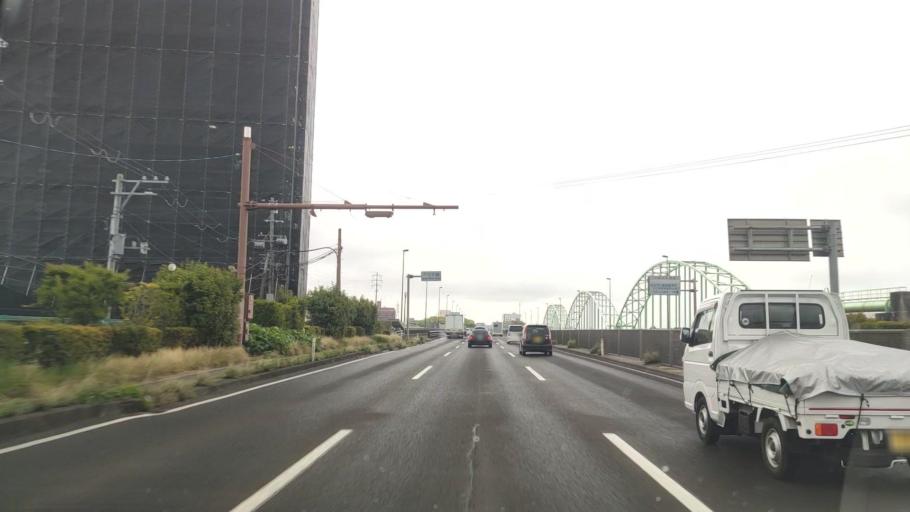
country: JP
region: Miyagi
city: Sendai
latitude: 38.2239
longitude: 140.8998
